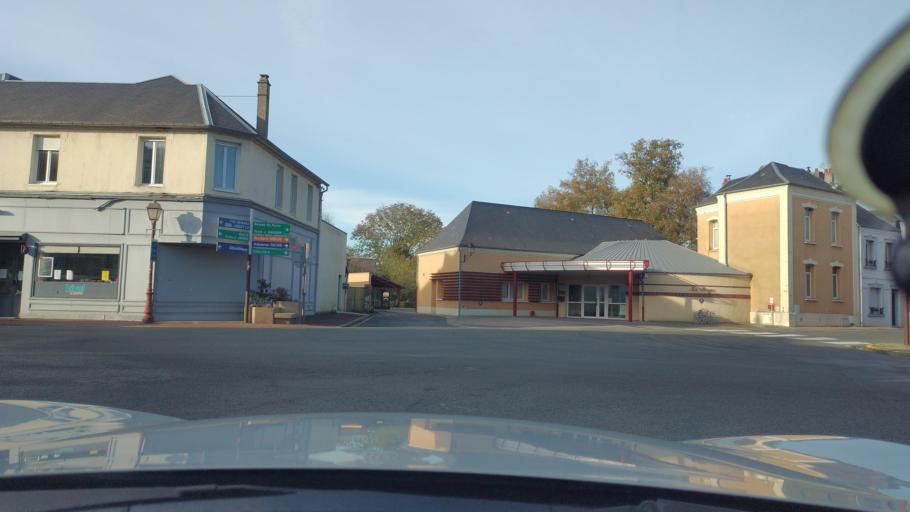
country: FR
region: Picardie
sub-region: Departement de la Somme
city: Fressenneville
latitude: 50.0673
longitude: 1.5762
